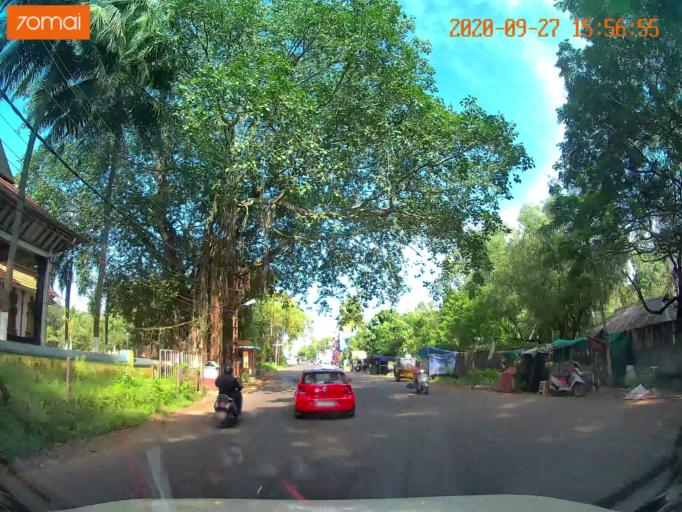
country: IN
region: Kerala
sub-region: Thrissur District
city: Trichur
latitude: 10.5178
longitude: 76.1830
